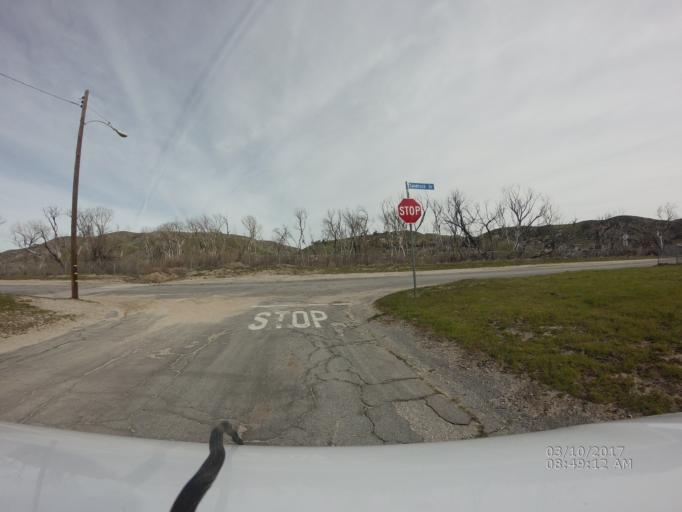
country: US
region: California
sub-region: Los Angeles County
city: Green Valley
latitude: 34.6622
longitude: -118.3930
